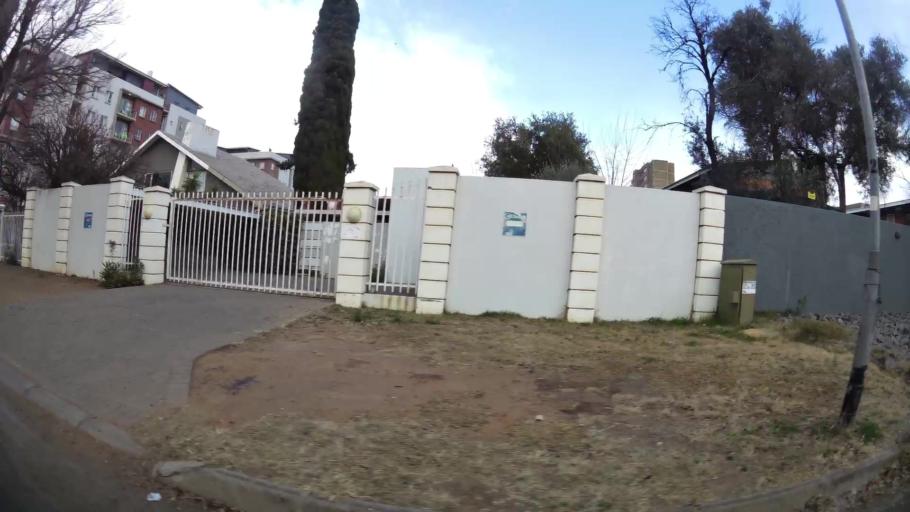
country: ZA
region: Orange Free State
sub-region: Mangaung Metropolitan Municipality
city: Bloemfontein
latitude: -29.1171
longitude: 26.1885
